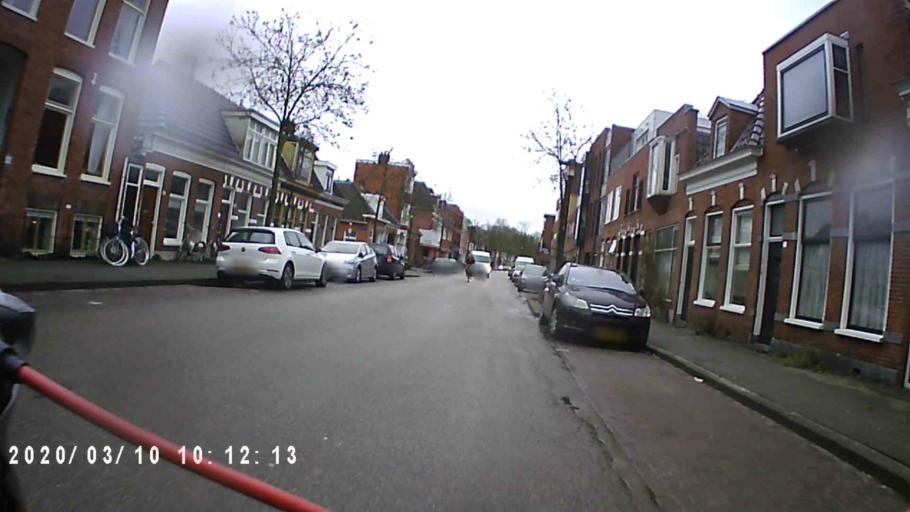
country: NL
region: Groningen
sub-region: Gemeente Groningen
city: Groningen
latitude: 53.2260
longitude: 6.5510
